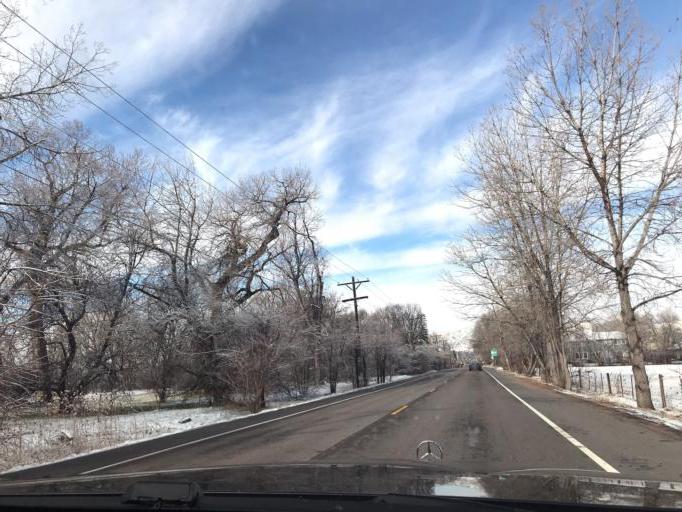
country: US
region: Colorado
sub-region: Boulder County
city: Boulder
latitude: 40.0001
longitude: -105.2187
